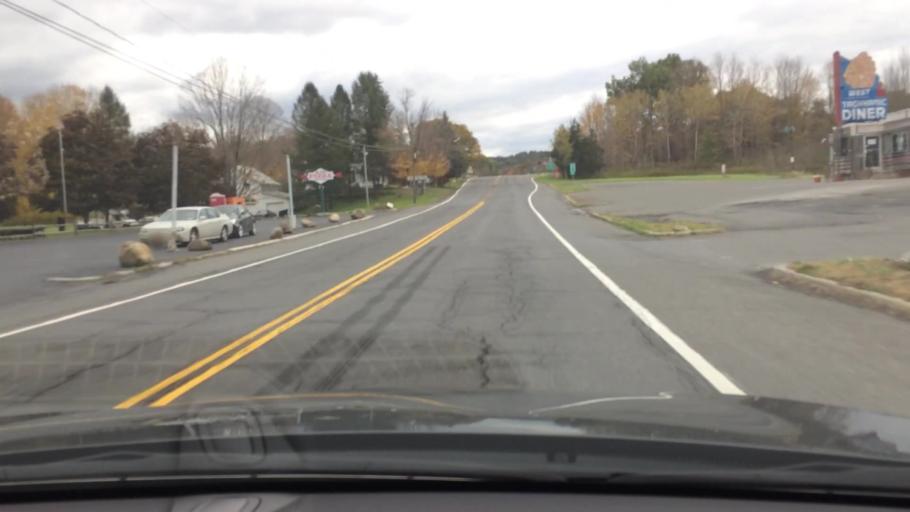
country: US
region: New York
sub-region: Columbia County
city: Philmont
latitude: 42.1201
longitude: -73.7176
